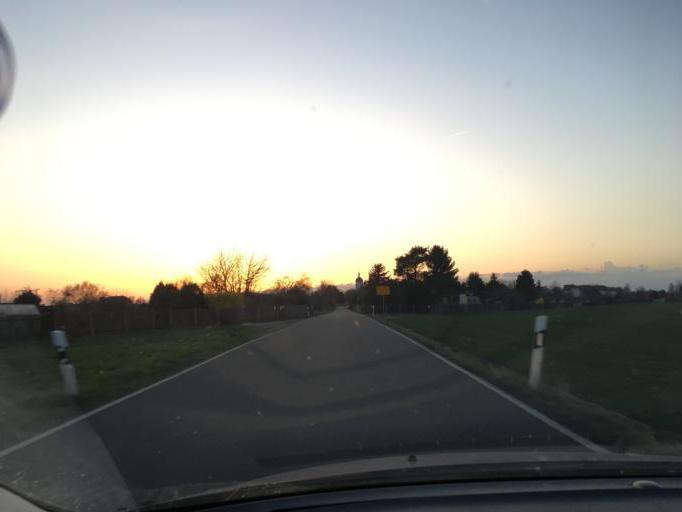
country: DE
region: Saxony
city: Borsdorf
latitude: 51.3328
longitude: 12.4974
